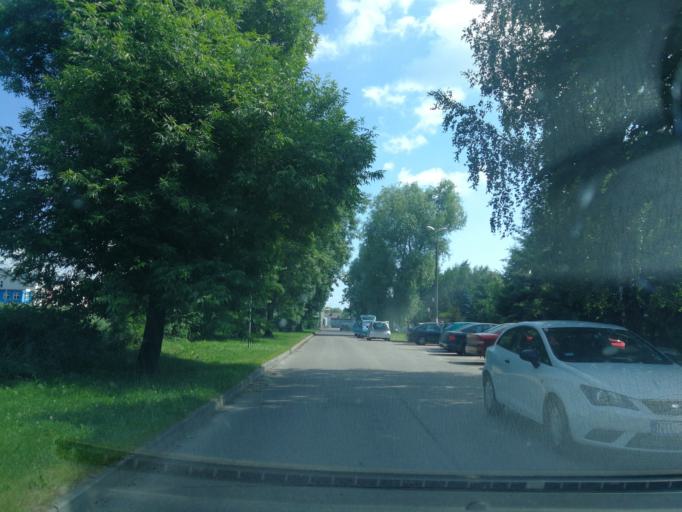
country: PL
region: Warmian-Masurian Voivodeship
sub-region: Powiat ilawski
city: Lubawa
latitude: 53.5003
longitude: 19.7516
